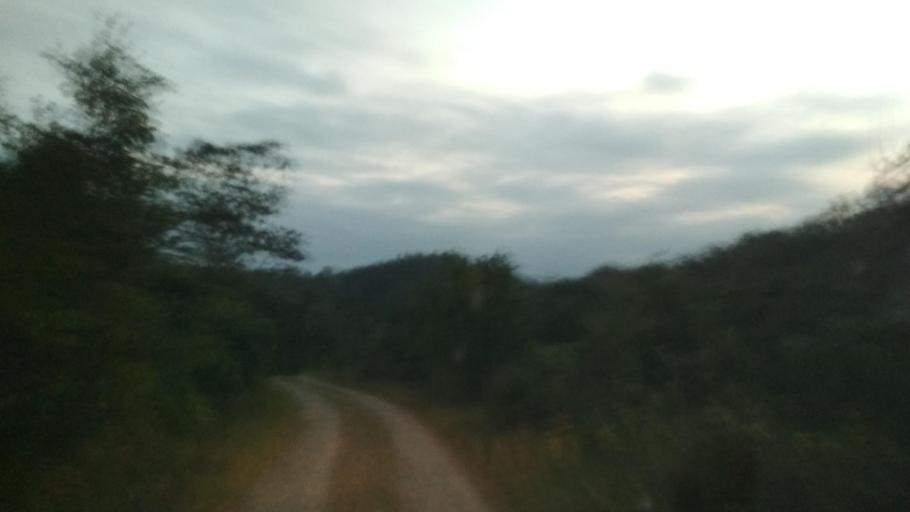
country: MX
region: Veracruz
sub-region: Poza Rica de Hidalgo
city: Arroyo del Maiz Uno
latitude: 20.4839
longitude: -97.3898
